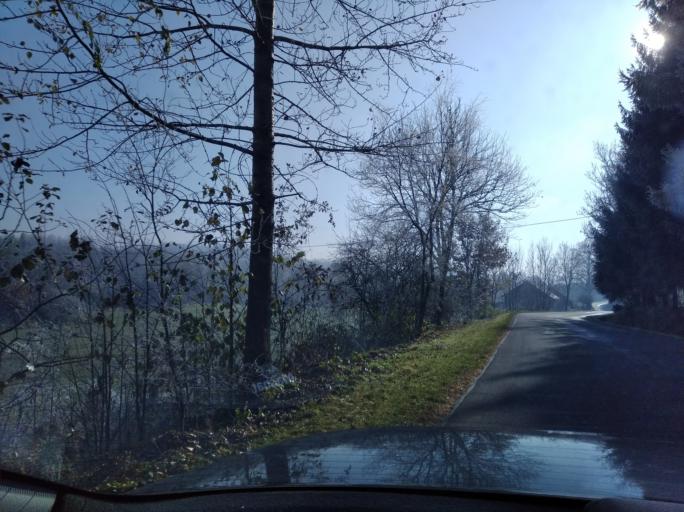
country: PL
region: Subcarpathian Voivodeship
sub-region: Powiat strzyzowski
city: Wysoka Strzyzowska
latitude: 49.8398
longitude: 21.7373
